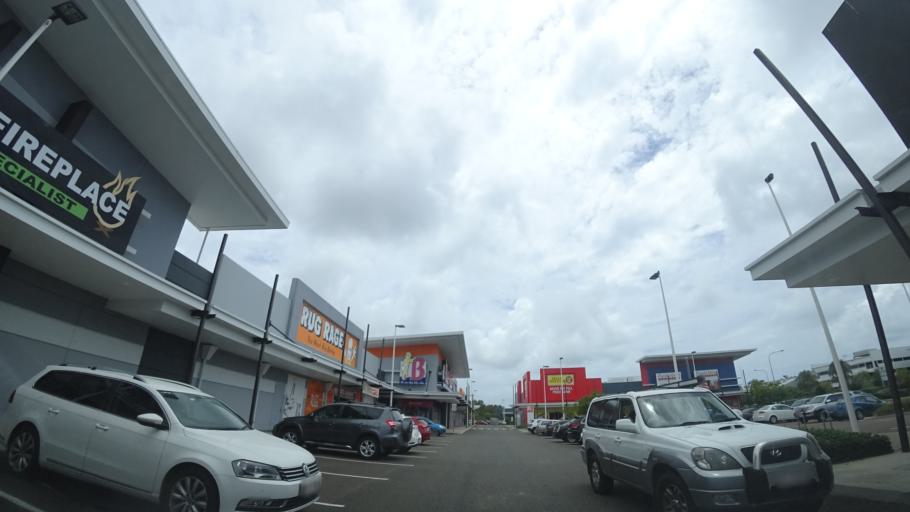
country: AU
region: Queensland
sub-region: Sunshine Coast
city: Dicky Beach
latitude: -26.7350
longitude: 153.1198
